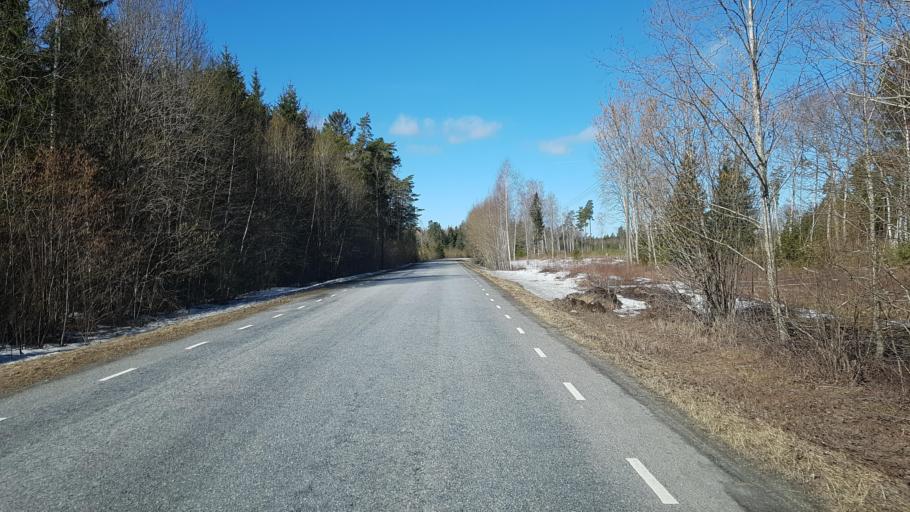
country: EE
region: Raplamaa
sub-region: Maerjamaa vald
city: Marjamaa
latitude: 58.8890
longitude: 24.4867
